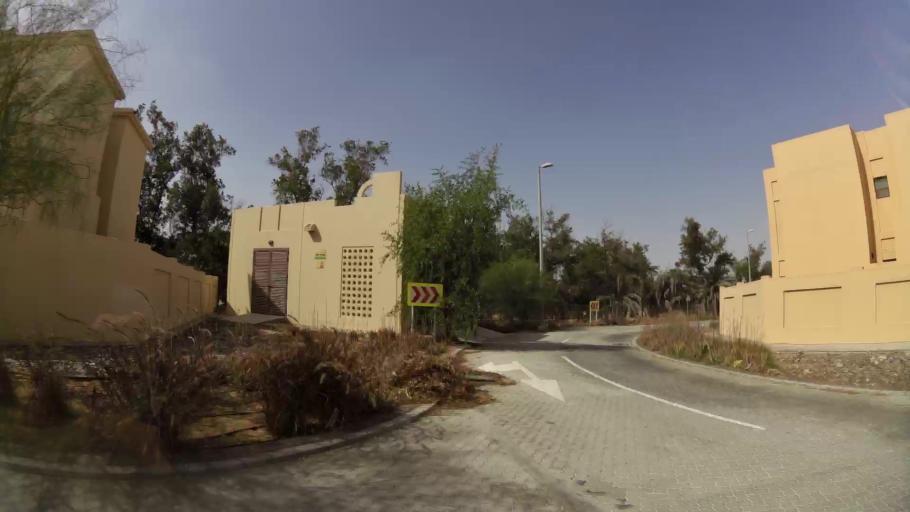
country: AE
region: Abu Dhabi
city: Abu Dhabi
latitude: 24.4103
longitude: 54.5332
